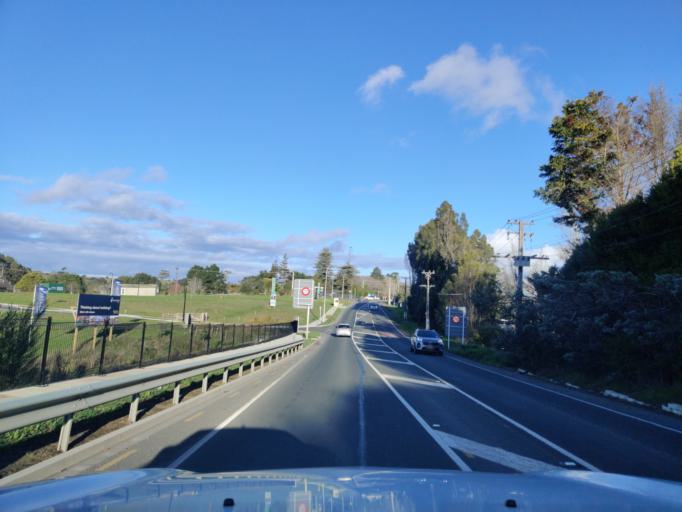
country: NZ
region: Auckland
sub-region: Auckland
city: Pakuranga
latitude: -36.9488
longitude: 174.9650
